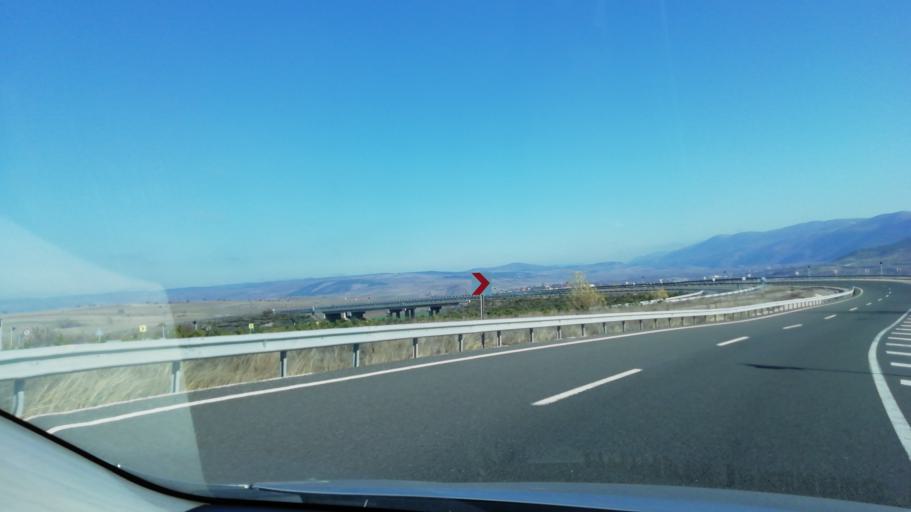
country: TR
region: Karabuk
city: Gozyeri
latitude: 40.8705
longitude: 32.5762
